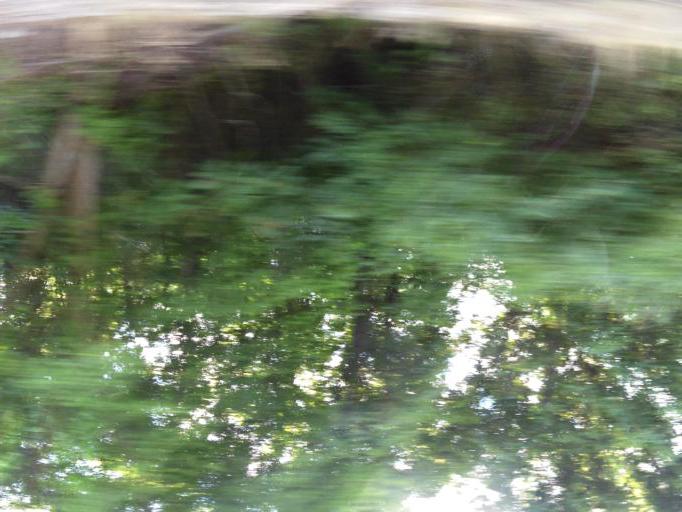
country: US
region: Missouri
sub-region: Saint Louis County
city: Wildwood
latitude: 38.6013
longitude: -90.6445
